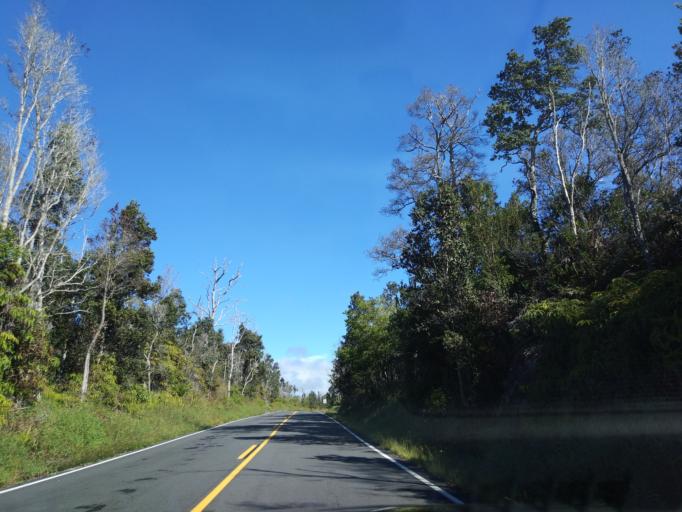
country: US
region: Hawaii
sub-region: Hawaii County
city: Volcano
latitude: 19.3716
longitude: -155.2284
